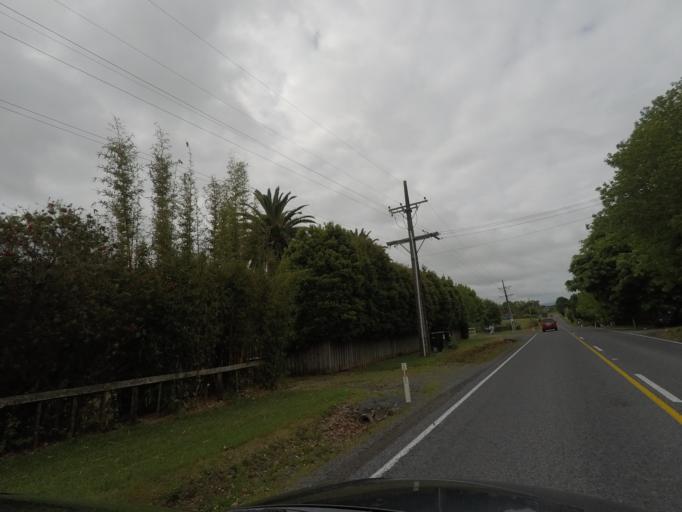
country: NZ
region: Auckland
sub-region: Auckland
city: Rosebank
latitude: -36.7961
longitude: 174.5740
